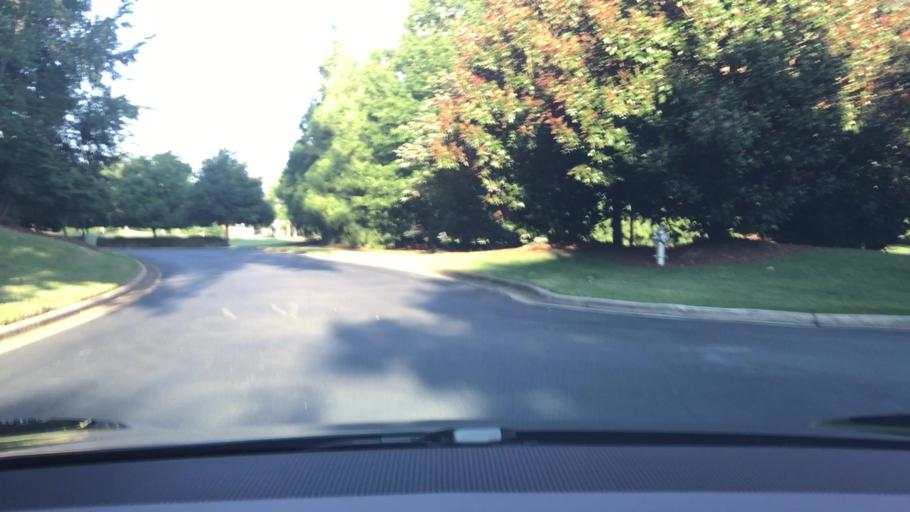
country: US
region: Georgia
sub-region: Gwinnett County
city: Suwanee
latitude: 34.0717
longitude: -84.1106
